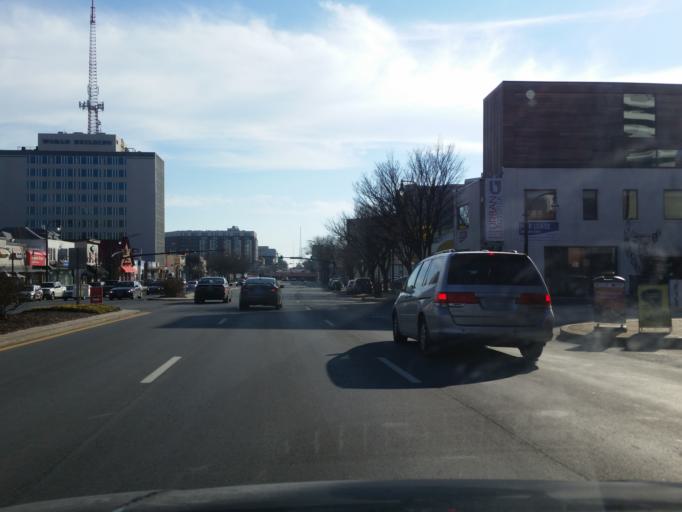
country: US
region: Maryland
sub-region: Montgomery County
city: Silver Spring
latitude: 38.9927
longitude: -77.0266
